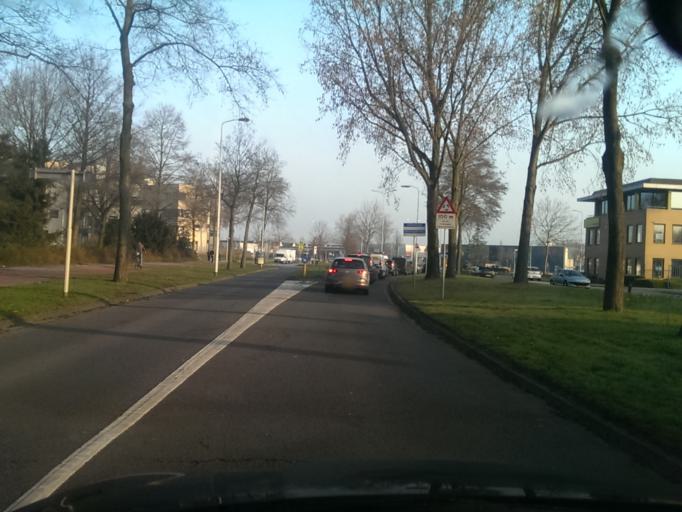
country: NL
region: North Brabant
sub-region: Gemeente Eindhoven
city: Meerhoven
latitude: 51.4260
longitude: 5.4430
